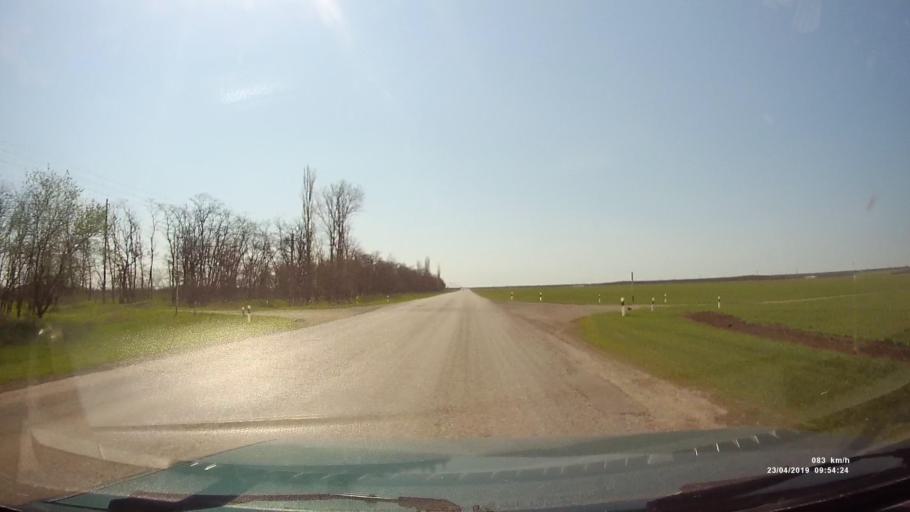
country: RU
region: Rostov
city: Orlovskiy
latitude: 46.8213
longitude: 42.0551
